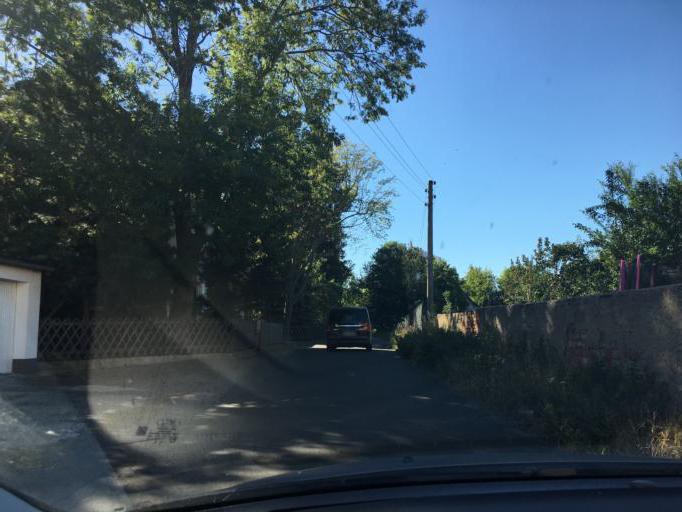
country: DE
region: Saxony
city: Borna
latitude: 51.0806
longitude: 12.5129
